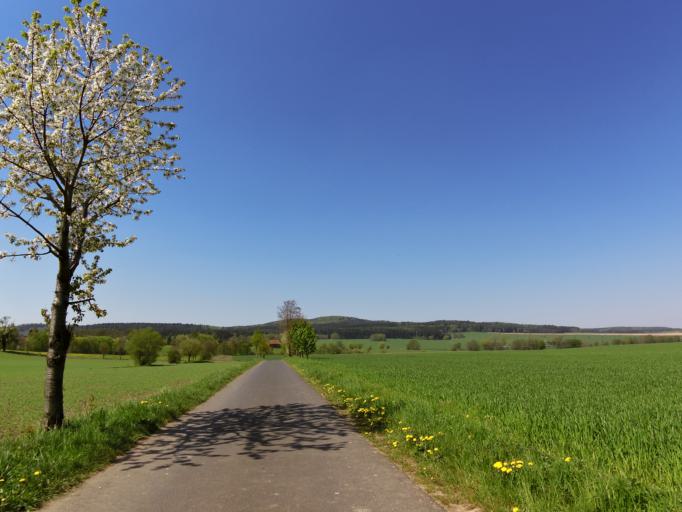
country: DE
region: Thuringia
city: Marksuhl
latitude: 50.8931
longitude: 10.2209
